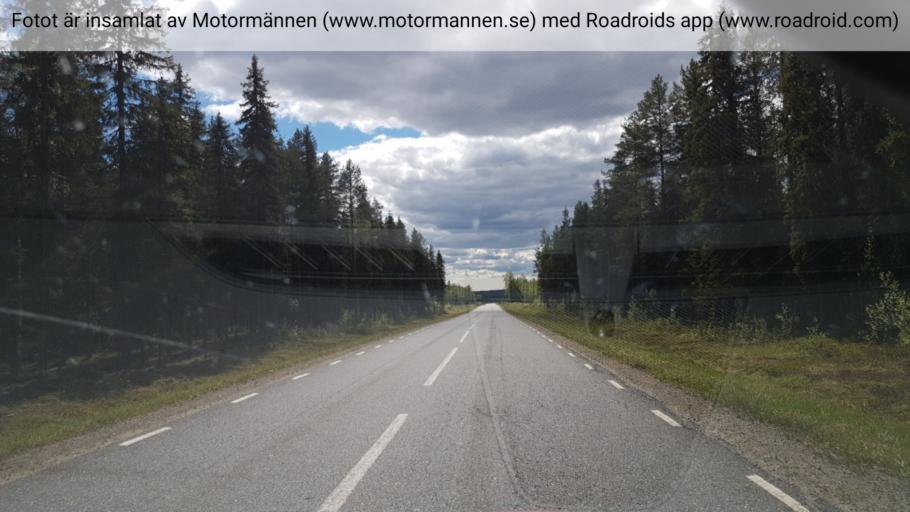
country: SE
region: Vaesterbotten
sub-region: Skelleftea Kommun
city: Langsele
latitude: 64.6665
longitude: 20.0183
